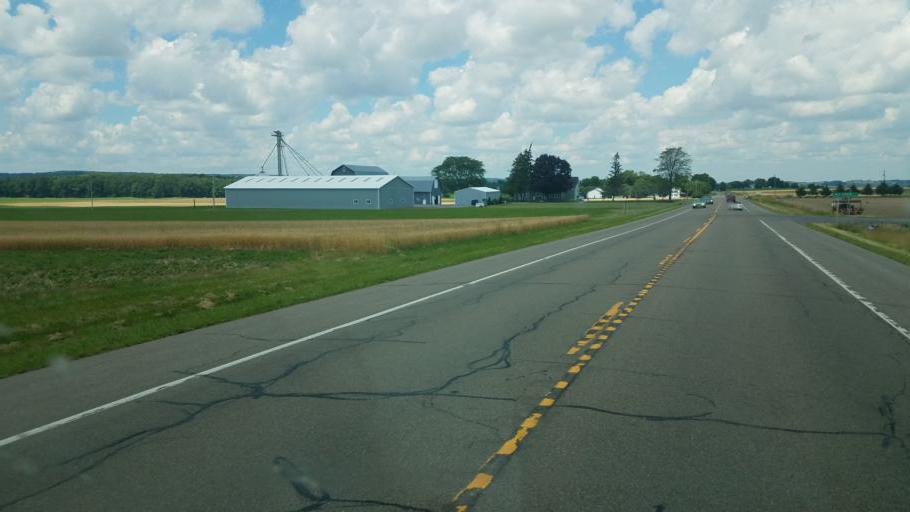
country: US
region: New York
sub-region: Yates County
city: Penn Yan
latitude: 42.6249
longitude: -77.0392
